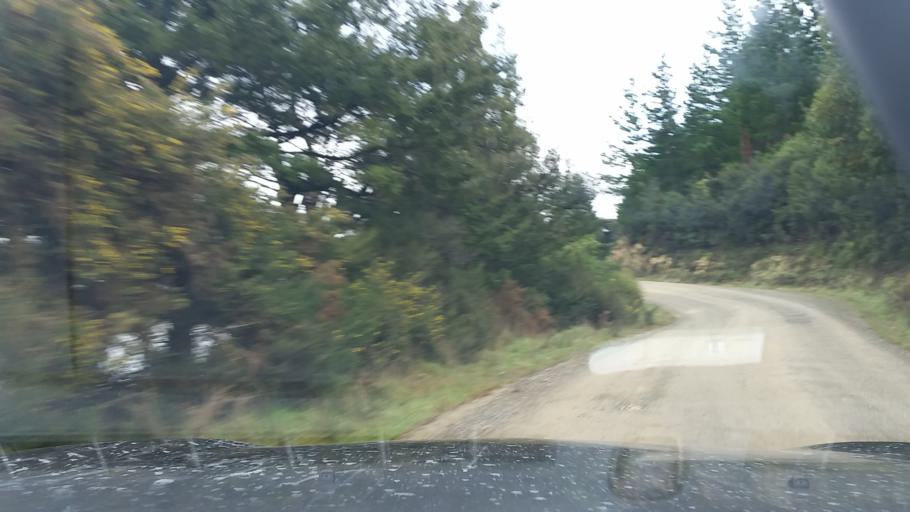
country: NZ
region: Marlborough
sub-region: Marlborough District
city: Picton
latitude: -41.1779
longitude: 174.0715
